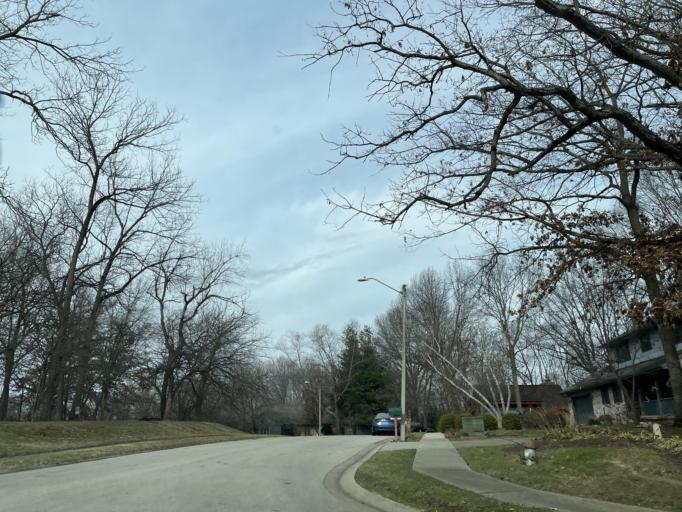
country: US
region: Illinois
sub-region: Sangamon County
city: Leland Grove
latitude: 39.8084
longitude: -89.7233
